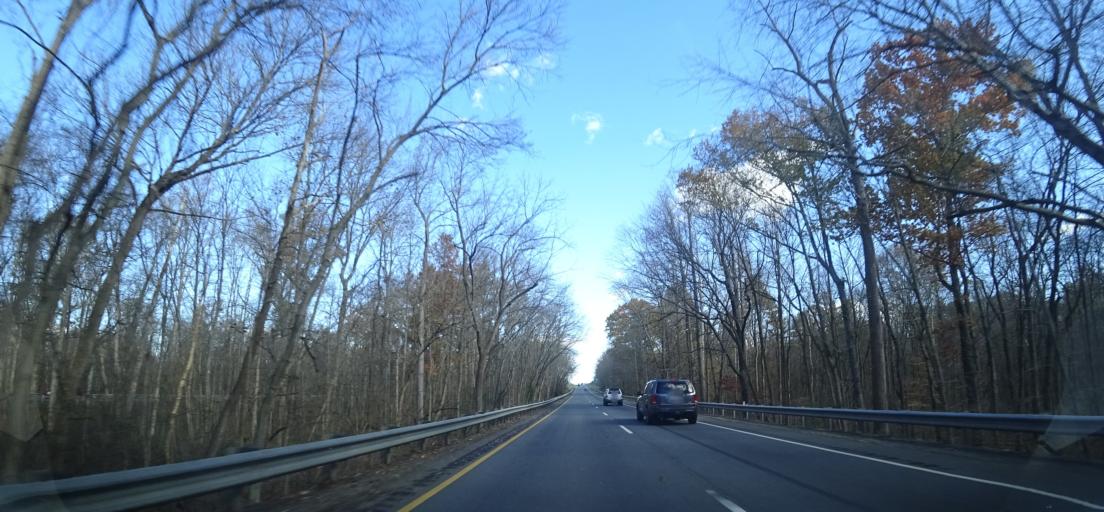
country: US
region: Virginia
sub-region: Culpeper County
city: Culpeper
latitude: 38.4614
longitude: -77.9658
